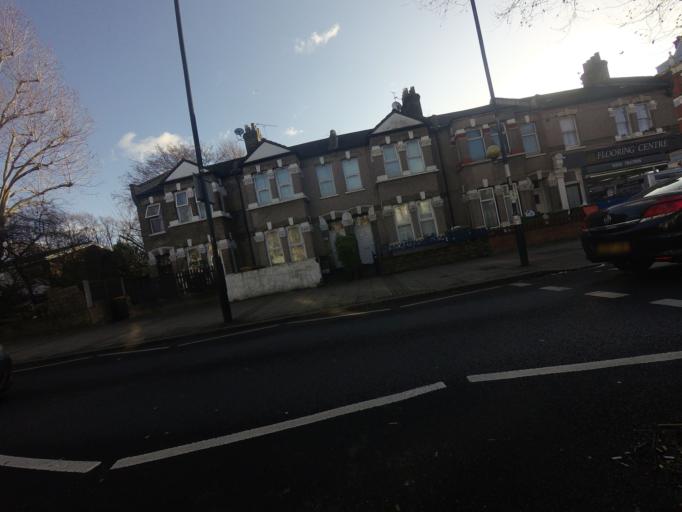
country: GB
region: England
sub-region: Greater London
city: East Ham
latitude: 51.5484
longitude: 0.0403
